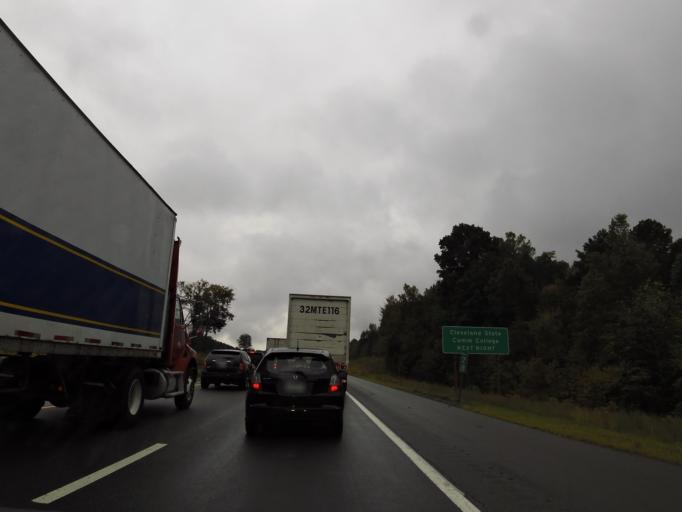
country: US
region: Tennessee
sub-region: Bradley County
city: Hopewell
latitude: 35.2292
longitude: -84.8556
